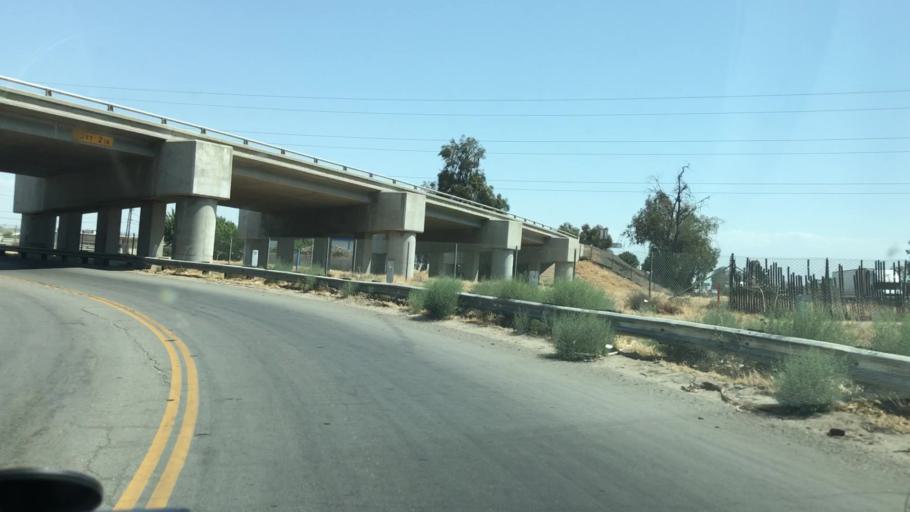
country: US
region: California
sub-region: Kern County
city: Oildale
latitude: 35.3989
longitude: -119.0444
